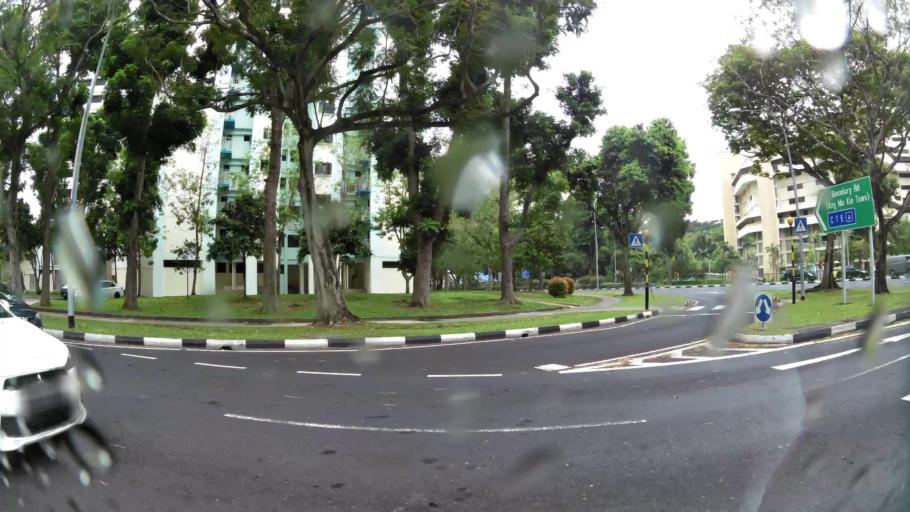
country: SG
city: Singapore
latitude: 1.3553
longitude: 103.8732
